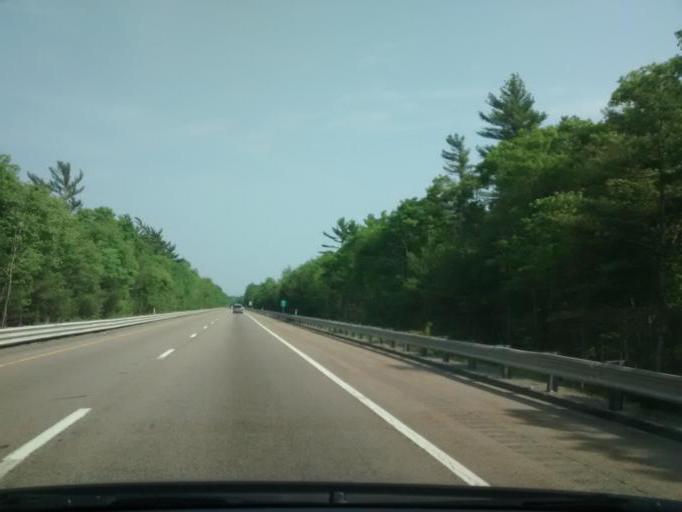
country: US
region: Massachusetts
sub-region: Plymouth County
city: West Wareham
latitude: 41.8237
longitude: -70.8078
